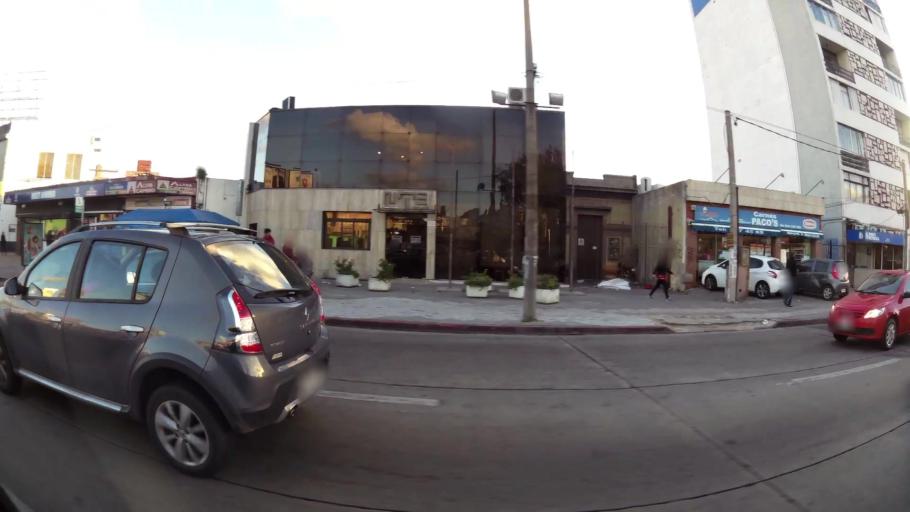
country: UY
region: Montevideo
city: Montevideo
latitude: -34.8870
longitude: -56.1304
